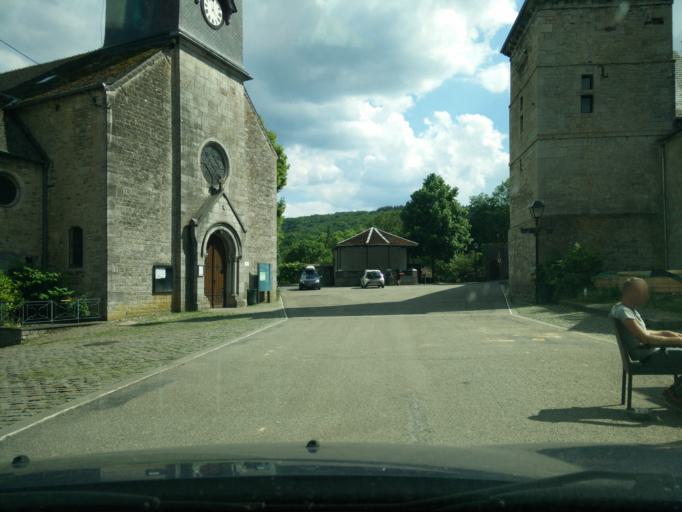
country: FR
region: Champagne-Ardenne
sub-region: Departement des Ardennes
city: Vireux-Molhain
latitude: 50.0804
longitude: 4.6342
